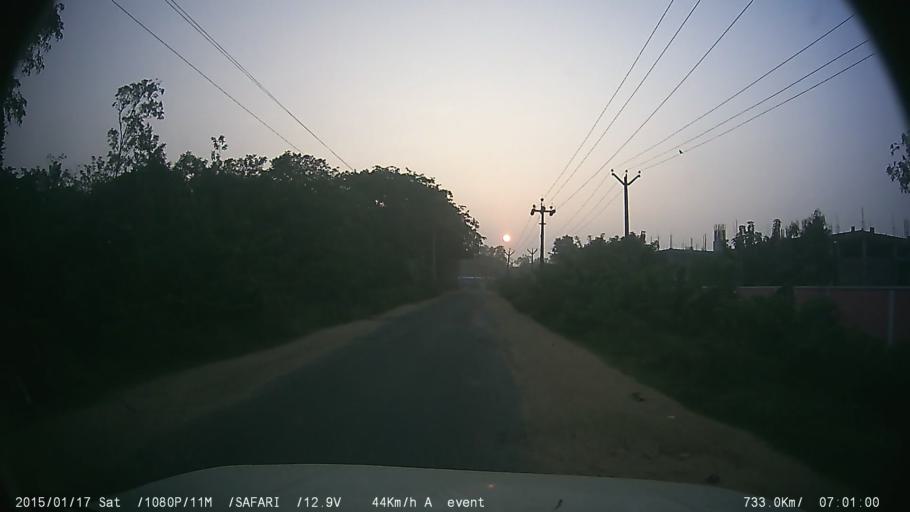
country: IN
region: Tamil Nadu
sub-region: Kancheepuram
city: Singapperumalkovil
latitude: 12.7957
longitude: 80.0167
